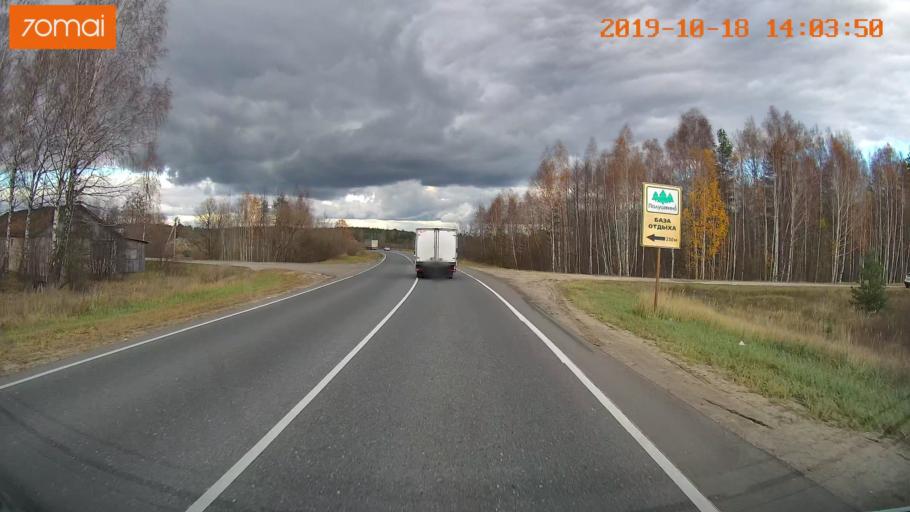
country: RU
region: Rjazan
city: Spas-Klepiki
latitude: 55.1196
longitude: 40.1319
